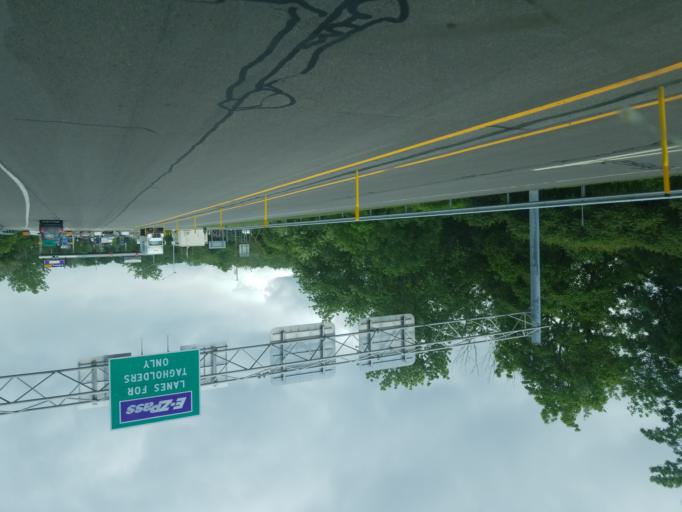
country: US
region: New York
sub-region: Ontario County
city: Phelps
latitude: 42.9529
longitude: -76.9808
